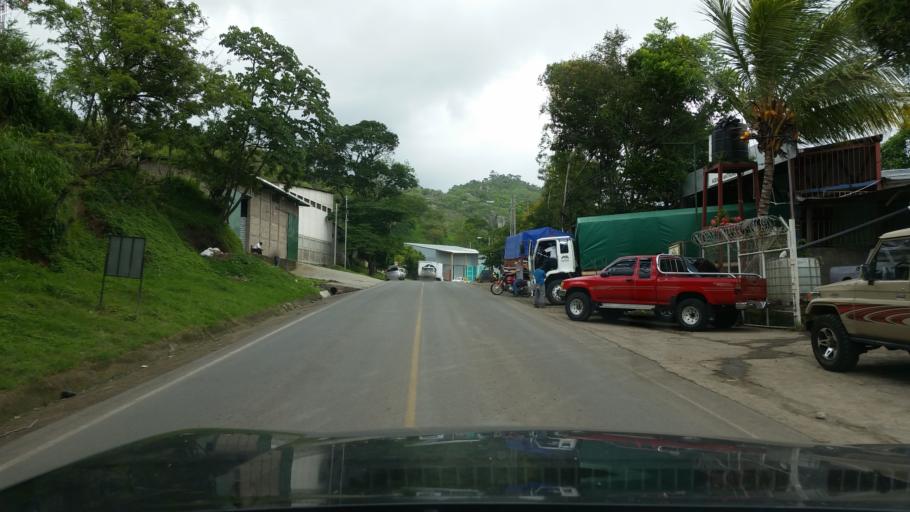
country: NI
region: Matagalpa
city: Matagalpa
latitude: 12.9407
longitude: -85.8984
